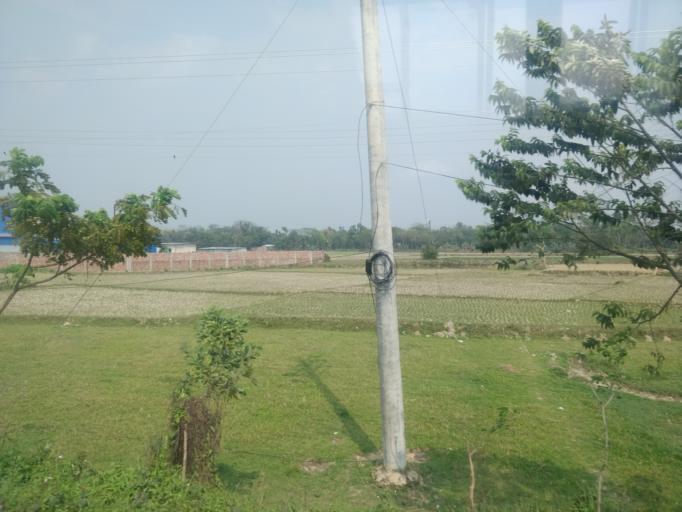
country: BD
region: Sylhet
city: Habiganj
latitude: 24.3173
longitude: 91.4359
